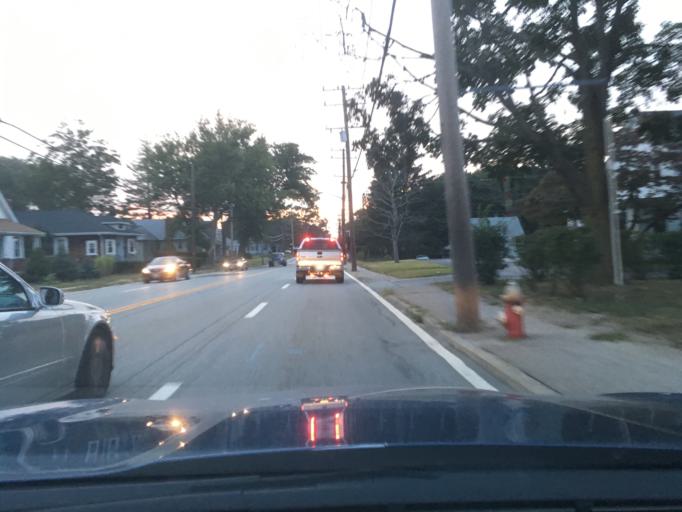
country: US
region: Rhode Island
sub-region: Kent County
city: Warwick
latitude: 41.7136
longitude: -71.4541
